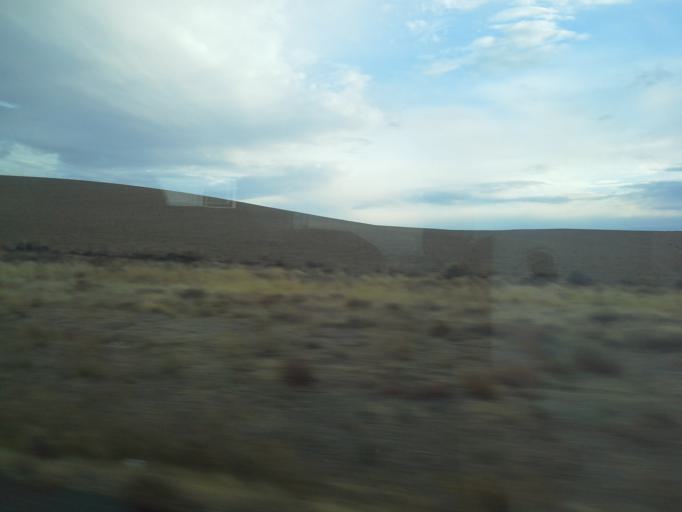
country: US
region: Oregon
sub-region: Umatilla County
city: Stanfield
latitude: 45.7443
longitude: -119.0976
